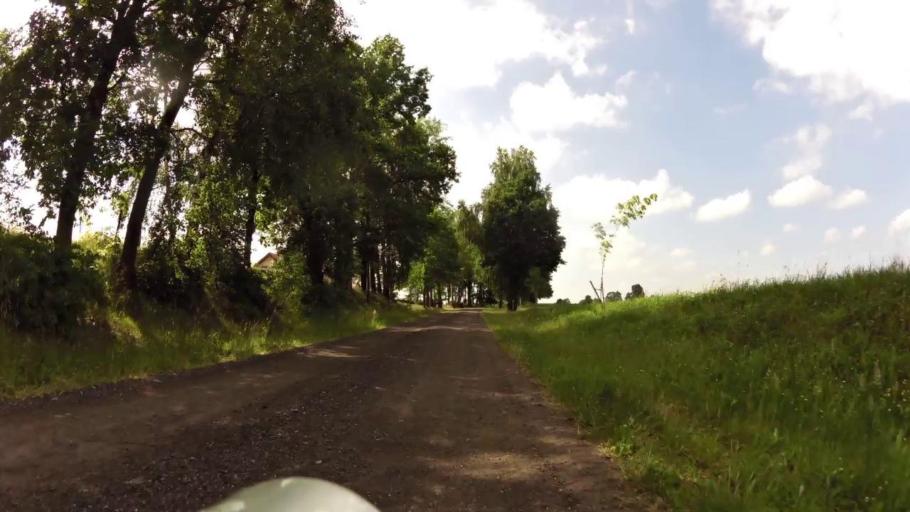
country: PL
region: West Pomeranian Voivodeship
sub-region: Powiat koszalinski
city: Bobolice
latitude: 53.9500
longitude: 16.6278
